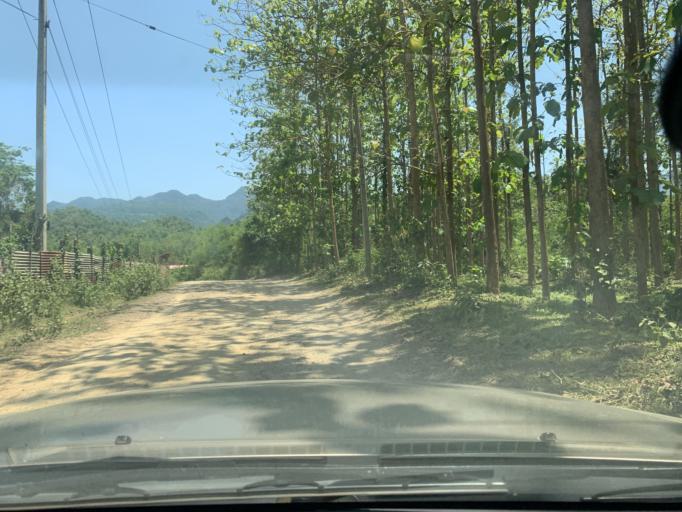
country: LA
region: Louangphabang
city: Louangphabang
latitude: 19.9049
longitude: 102.2422
